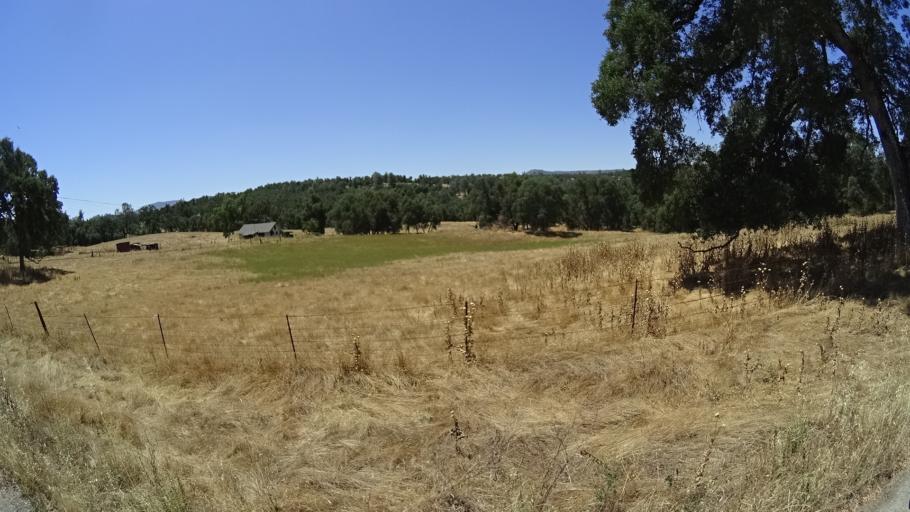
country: US
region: California
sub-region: Calaveras County
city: Angels Camp
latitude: 38.1095
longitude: -120.6092
